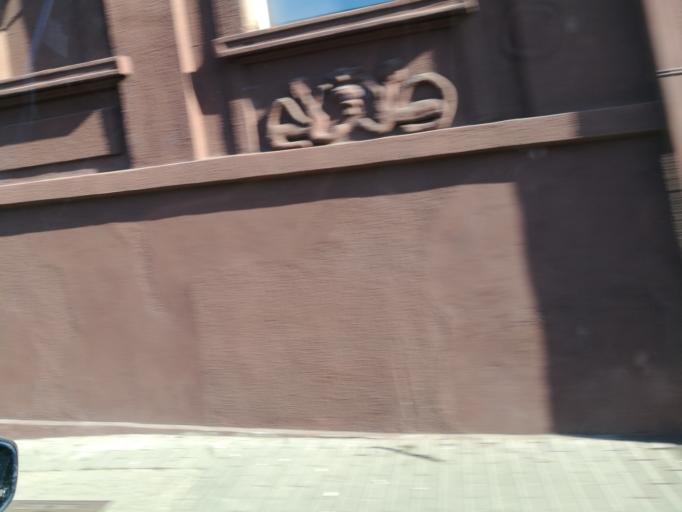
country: RO
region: Iasi
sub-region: Municipiul Iasi
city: Iasi
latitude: 47.1726
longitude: 27.5629
